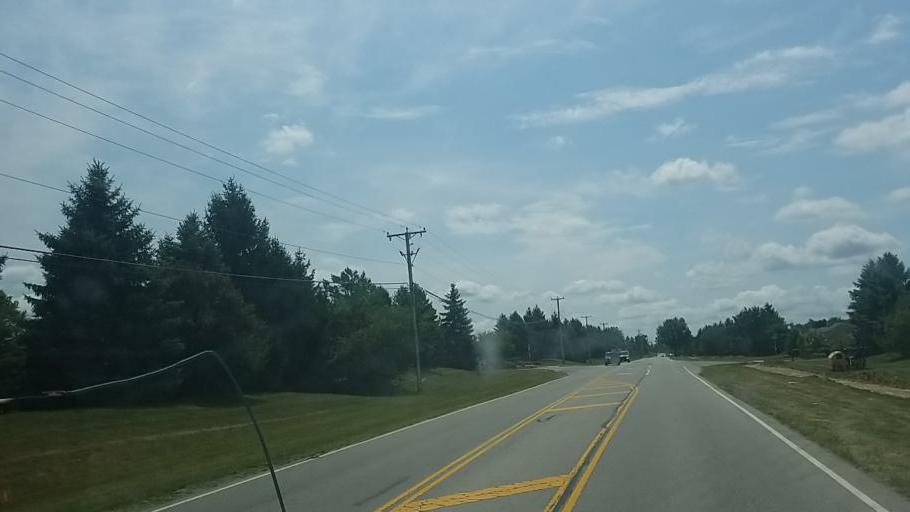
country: US
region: Ohio
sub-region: Franklin County
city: Reynoldsburg
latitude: 40.0079
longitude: -82.7664
